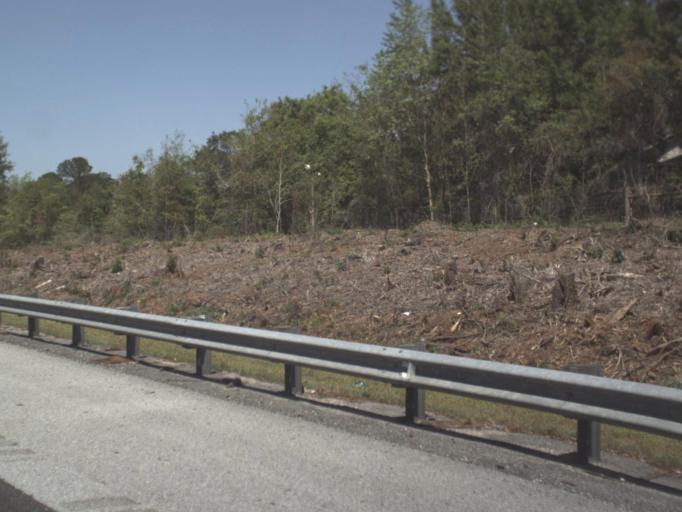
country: US
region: Florida
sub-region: Escambia County
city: Ferry Pass
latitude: 30.5023
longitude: -87.1749
